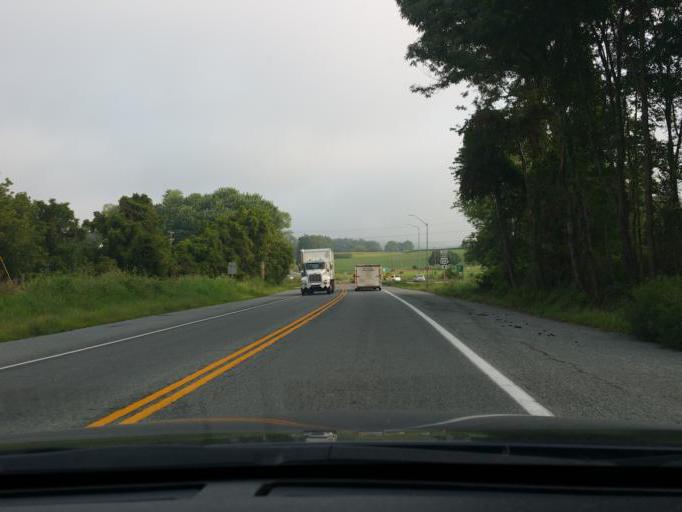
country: US
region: Maryland
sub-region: Cecil County
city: Rising Sun
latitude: 39.6946
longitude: -76.0796
